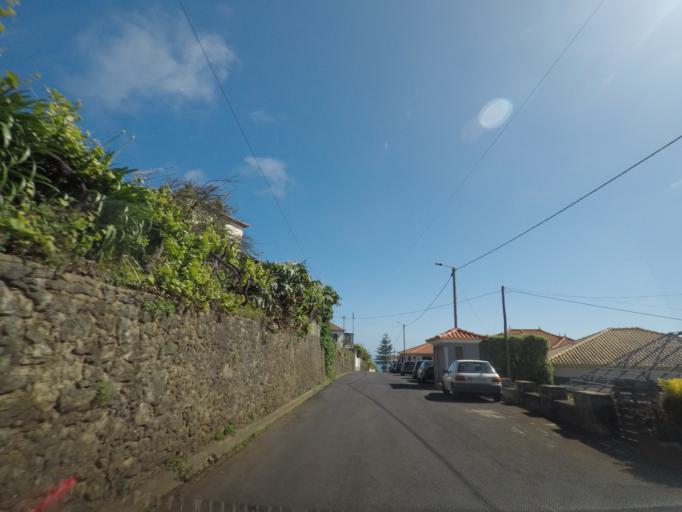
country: PT
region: Madeira
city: Ponta do Sol
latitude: 32.6938
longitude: -17.0964
